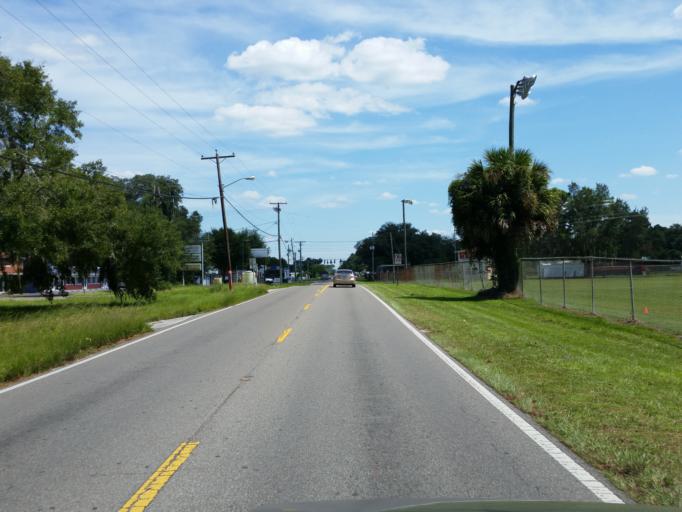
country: US
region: Florida
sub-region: Pasco County
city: Zephyrhills North
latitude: 28.2518
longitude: -82.1826
